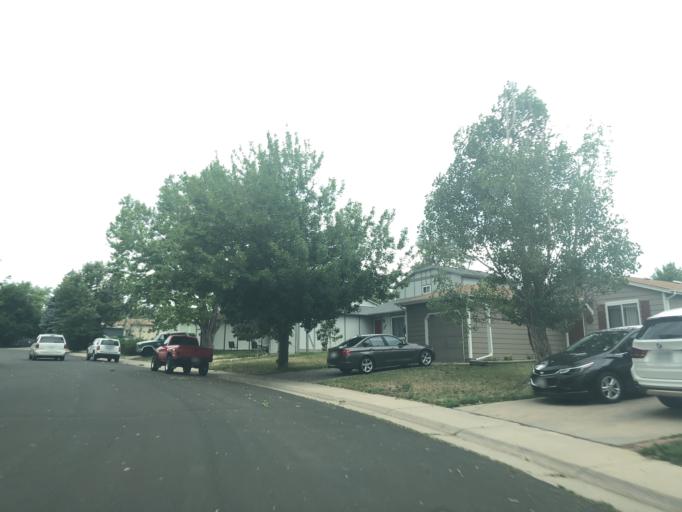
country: US
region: Colorado
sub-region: Arapahoe County
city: Dove Valley
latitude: 39.6318
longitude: -104.7852
